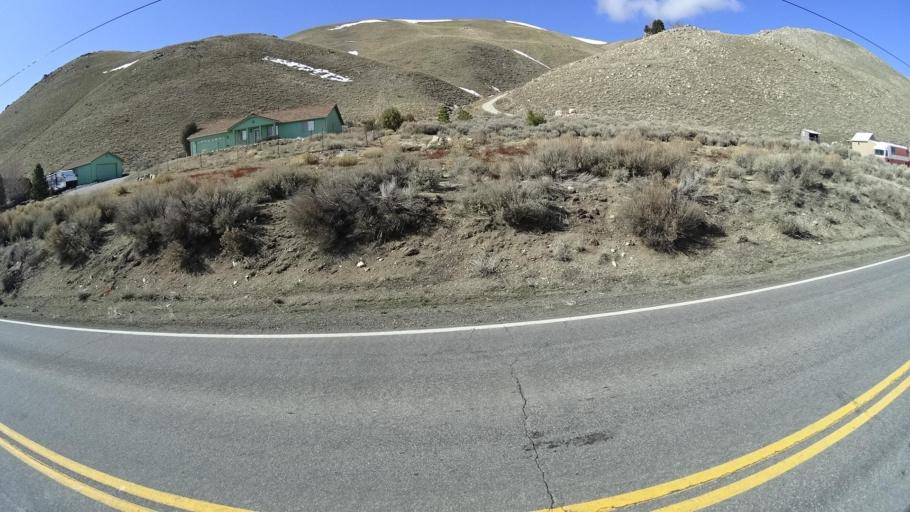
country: US
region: Nevada
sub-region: Washoe County
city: Cold Springs
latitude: 39.6381
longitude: -119.9219
